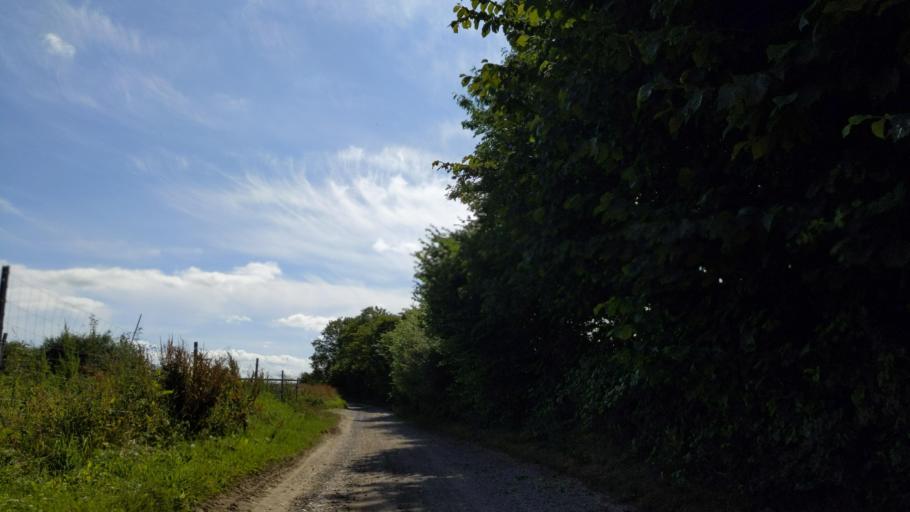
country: DE
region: Schleswig-Holstein
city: Susel
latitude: 54.1163
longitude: 10.7383
